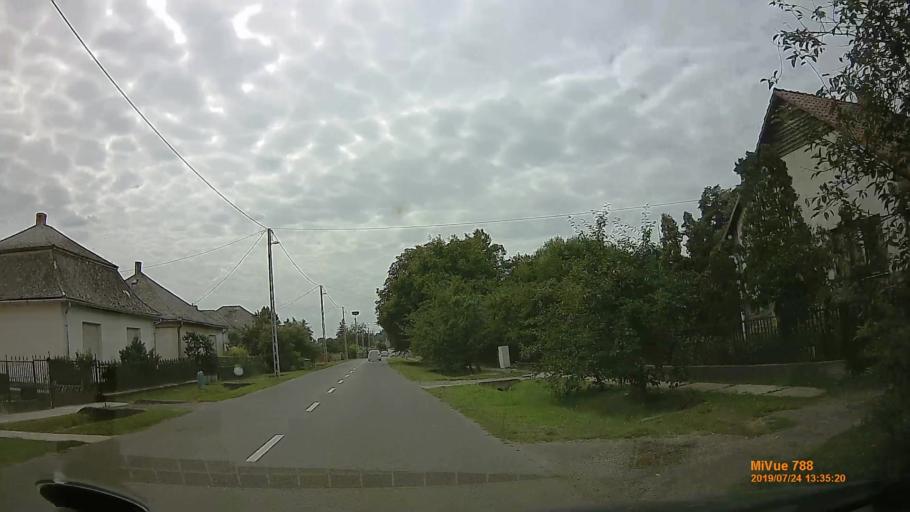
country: HU
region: Szabolcs-Szatmar-Bereg
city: Aranyosapati
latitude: 48.2267
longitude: 22.2938
